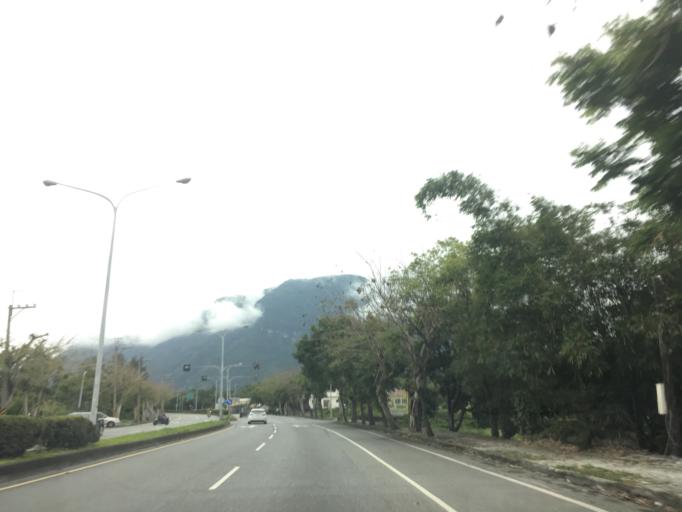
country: TW
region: Taiwan
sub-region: Hualien
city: Hualian
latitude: 24.1272
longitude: 121.6485
